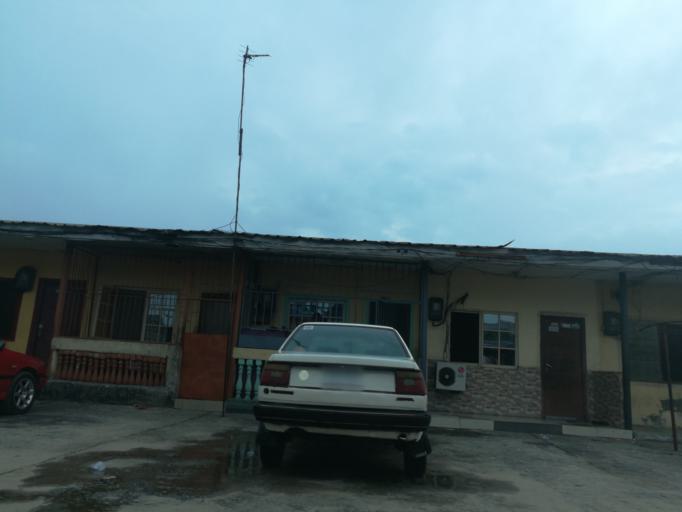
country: NG
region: Rivers
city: Port Harcourt
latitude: 4.7594
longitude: 7.0148
